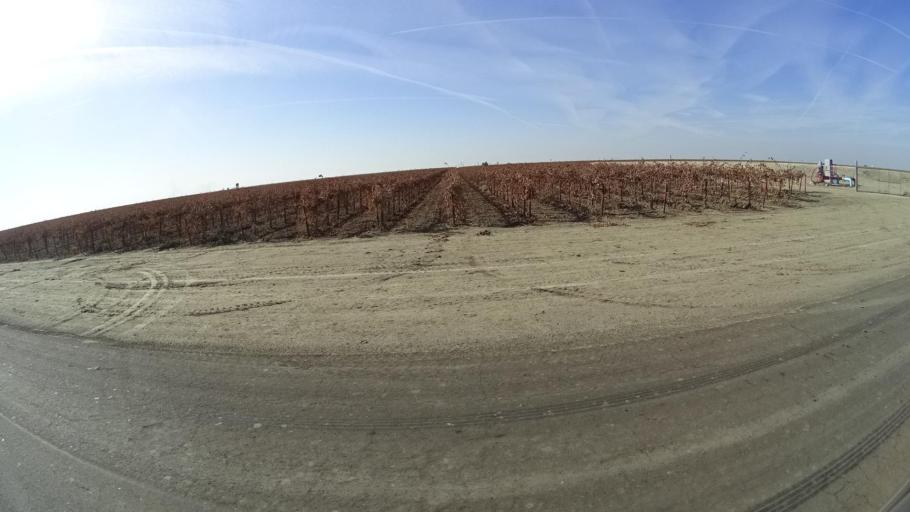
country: US
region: California
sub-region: Kern County
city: Wasco
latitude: 35.6956
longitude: -119.3839
